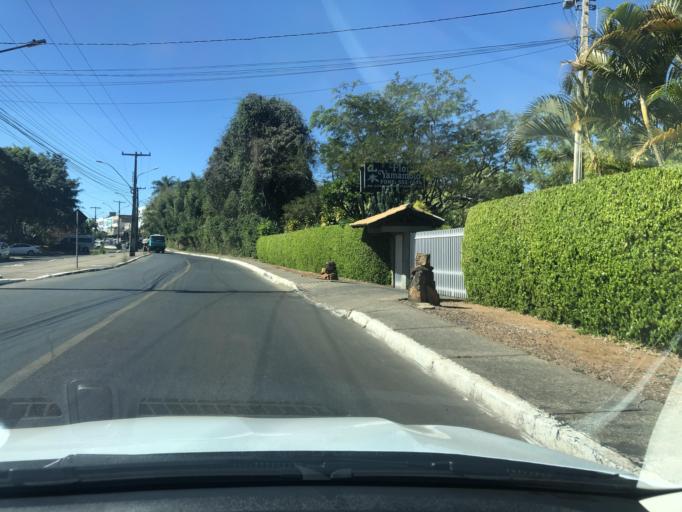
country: BR
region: Federal District
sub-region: Brasilia
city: Brasilia
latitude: -15.8733
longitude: -47.9663
